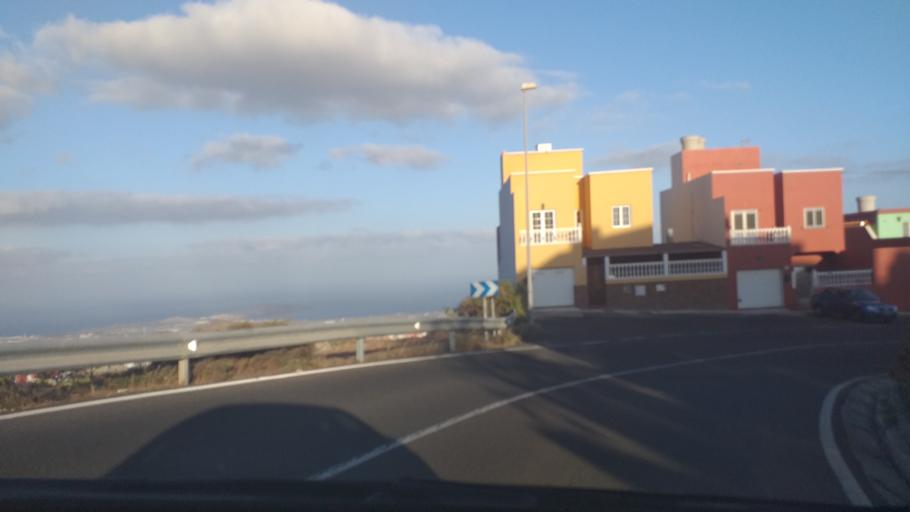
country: ES
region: Canary Islands
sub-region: Provincia de Las Palmas
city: Ingenio
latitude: 27.9224
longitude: -15.4490
